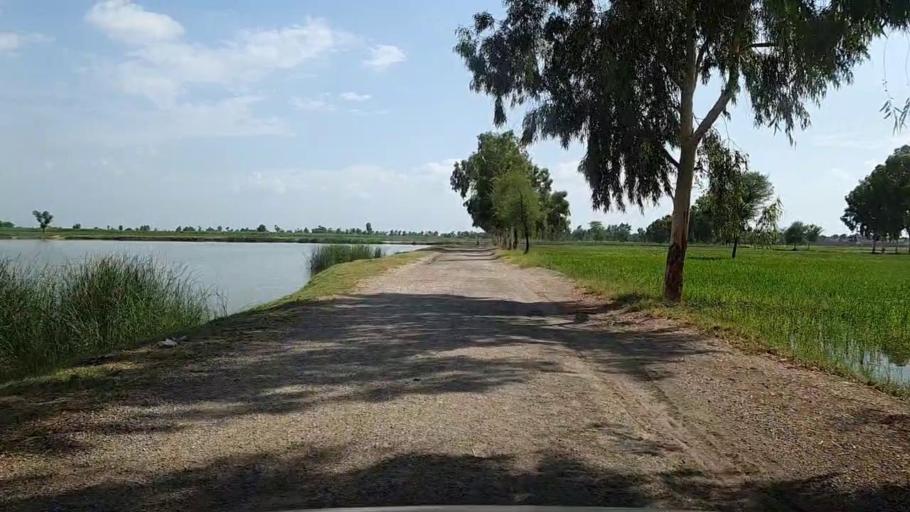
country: PK
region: Sindh
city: Bhiria
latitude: 26.9167
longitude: 68.2300
